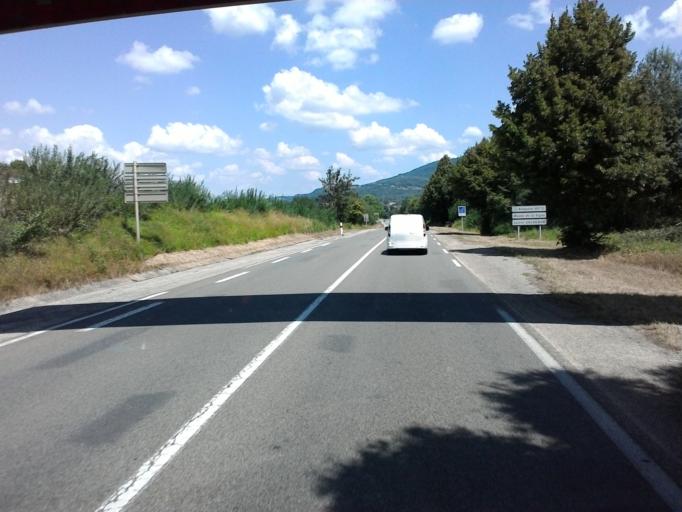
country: FR
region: Bourgogne
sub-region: Departement de Saone-et-Loire
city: Cuiseaux
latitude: 46.4842
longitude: 5.3696
